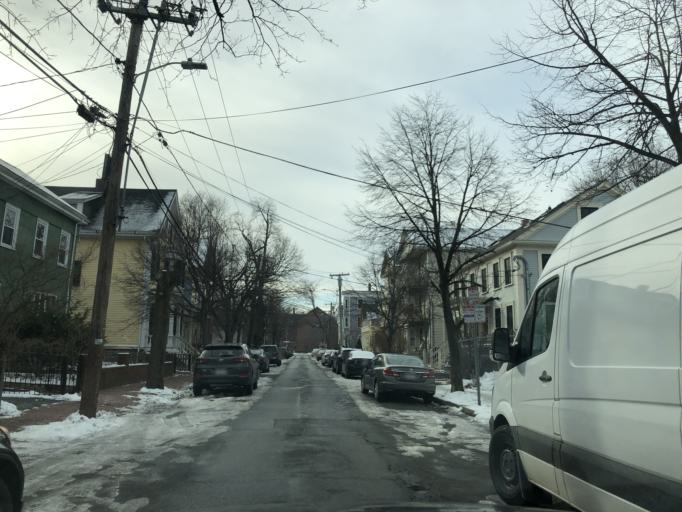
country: US
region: Massachusetts
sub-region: Middlesex County
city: Cambridge
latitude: 42.3701
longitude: -71.0992
